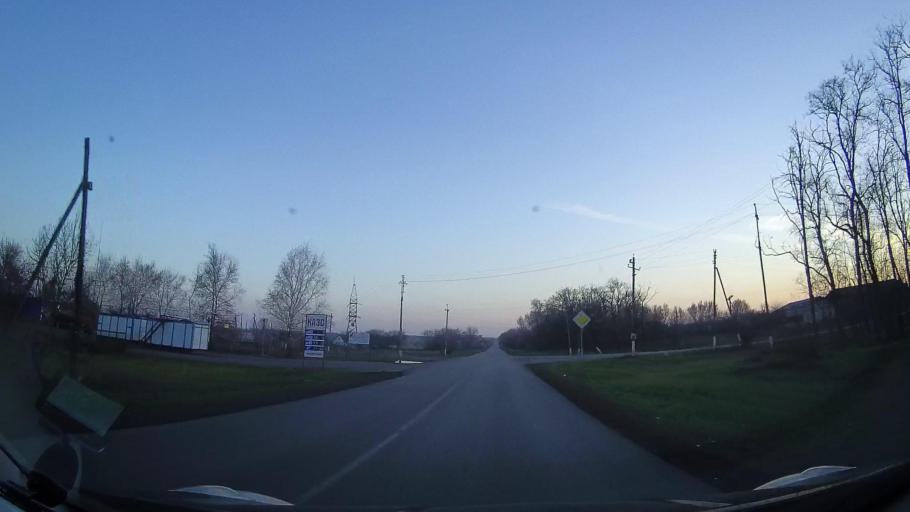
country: RU
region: Rostov
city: Zernograd
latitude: 47.0455
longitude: 40.3915
